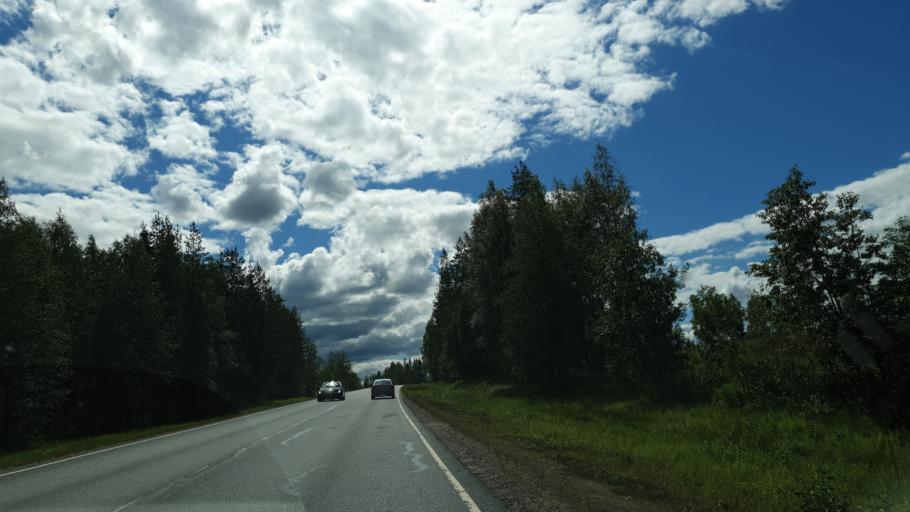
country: FI
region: North Karelia
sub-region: Pielisen Karjala
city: Valtimo
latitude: 63.4087
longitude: 28.7767
